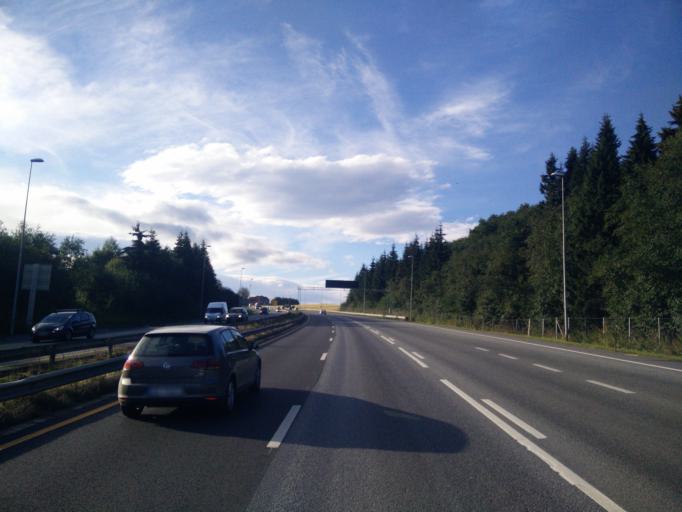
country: NO
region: Sor-Trondelag
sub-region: Trondheim
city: Trondheim
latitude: 63.3809
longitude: 10.3746
